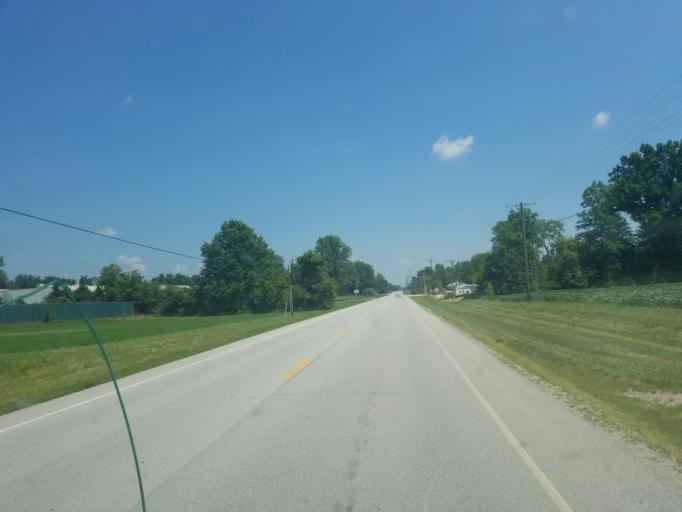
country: US
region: Ohio
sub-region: Auglaize County
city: Saint Marys
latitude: 40.5469
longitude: -84.3644
